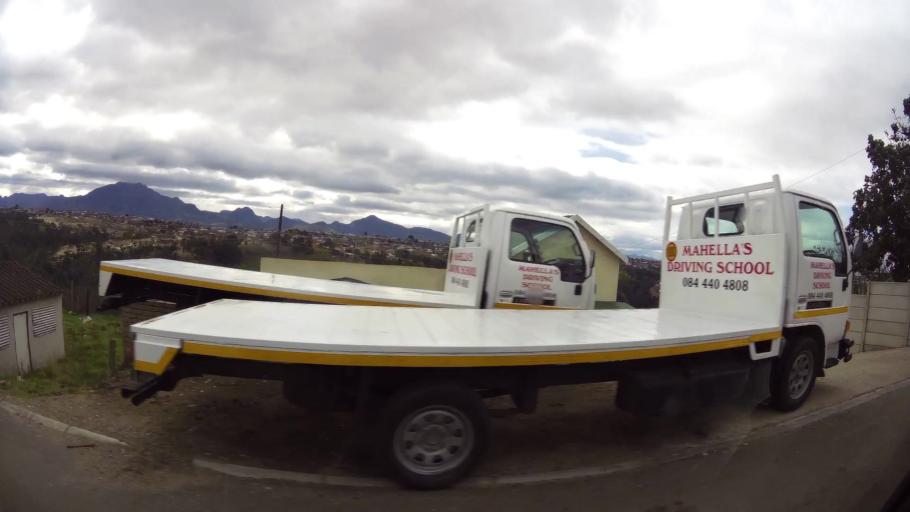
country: ZA
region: Western Cape
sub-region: Eden District Municipality
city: George
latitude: -34.0137
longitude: 22.4785
